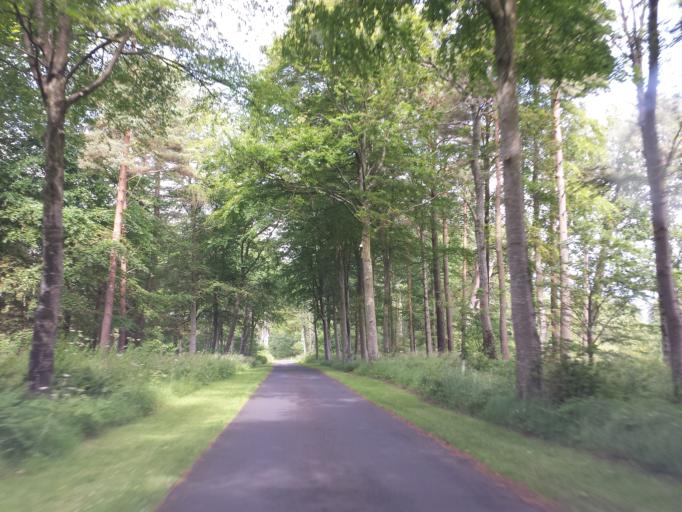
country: GB
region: Scotland
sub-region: South Ayrshire
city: Maybole
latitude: 55.3528
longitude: -4.7780
